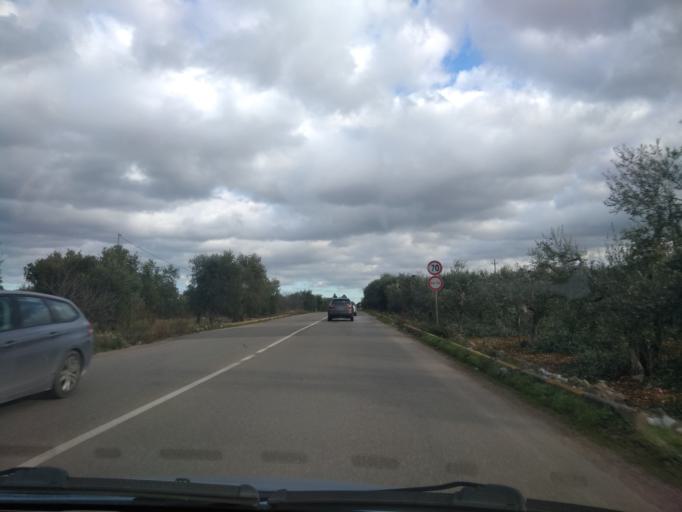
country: IT
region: Apulia
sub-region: Provincia di Bari
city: Adelfia
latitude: 41.0031
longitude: 16.8984
